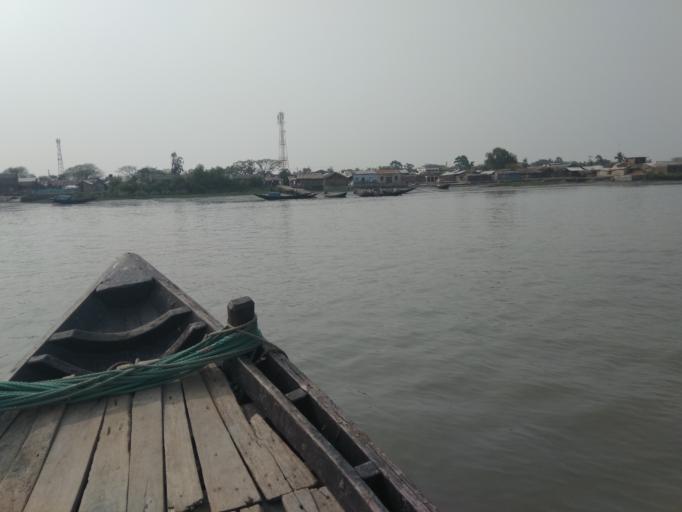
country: IN
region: West Bengal
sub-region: North 24 Parganas
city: Taki
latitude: 22.3469
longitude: 89.2046
